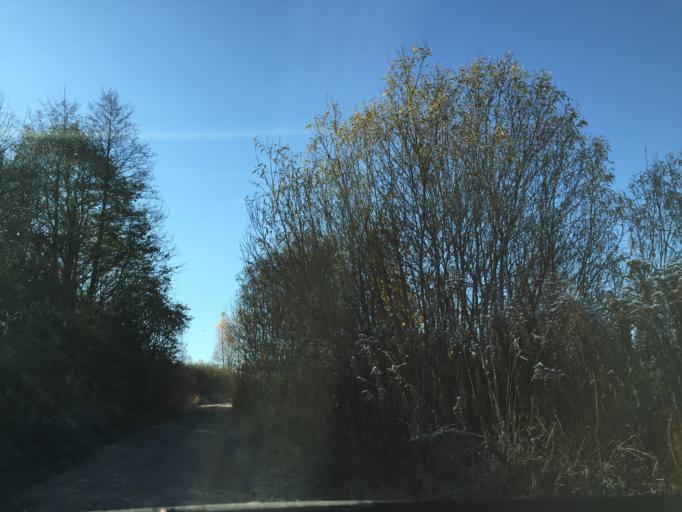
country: LV
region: Aizkraukles Rajons
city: Aizkraukle
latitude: 56.7094
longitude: 25.3000
